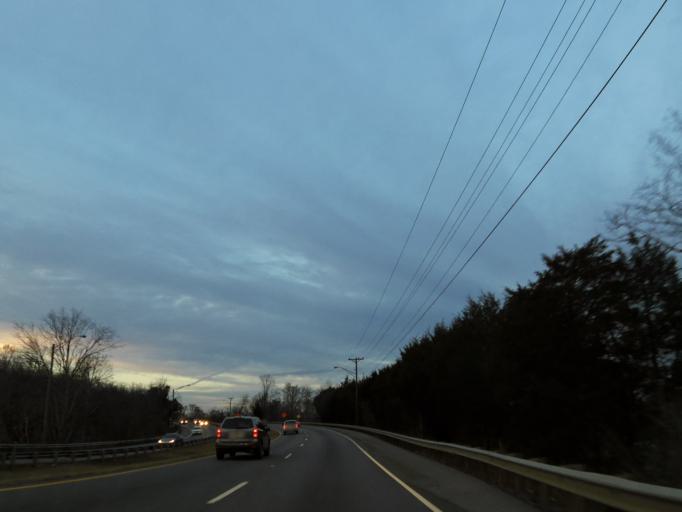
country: US
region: Tennessee
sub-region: Knox County
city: Knoxville
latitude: 35.8927
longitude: -83.9526
